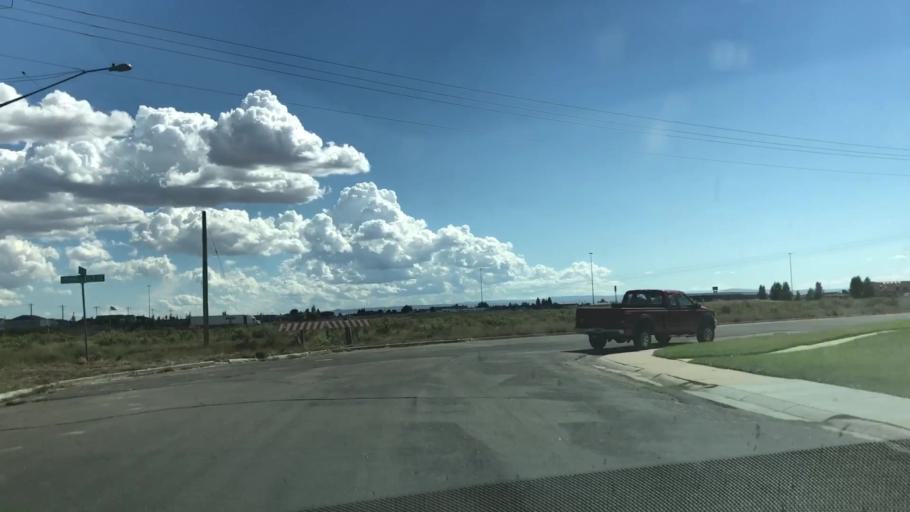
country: US
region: Wyoming
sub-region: Albany County
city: Laramie
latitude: 41.3026
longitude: -105.5880
